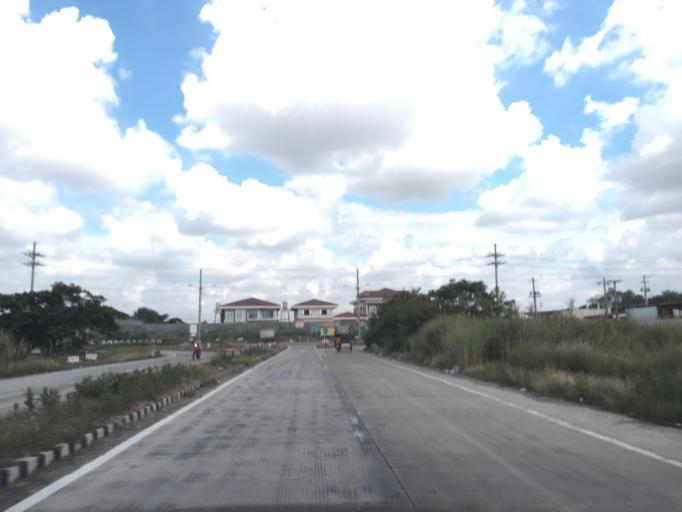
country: PH
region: Central Luzon
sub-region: Province of Tarlac
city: Salcedo
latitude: 15.8703
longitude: 120.6041
